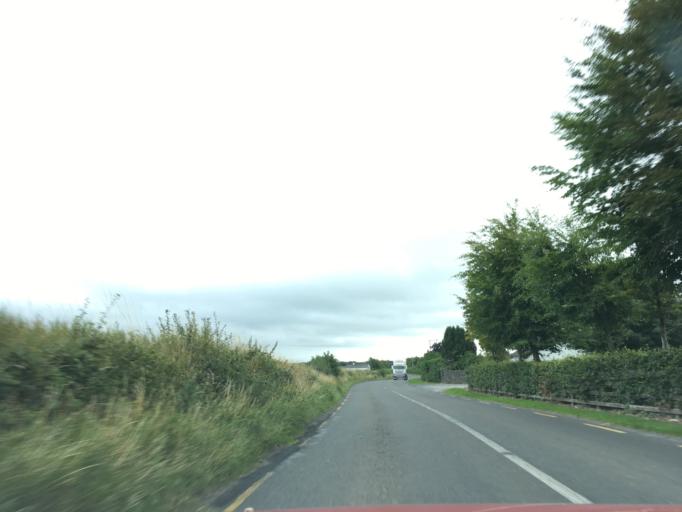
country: IE
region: Munster
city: Cashel
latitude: 52.4598
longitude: -7.8228
